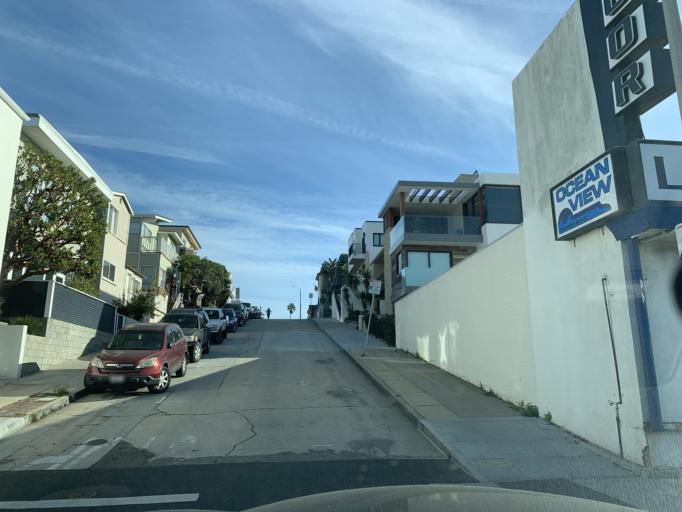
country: US
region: California
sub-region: Los Angeles County
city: Manhattan Beach
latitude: 33.8763
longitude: -118.4065
